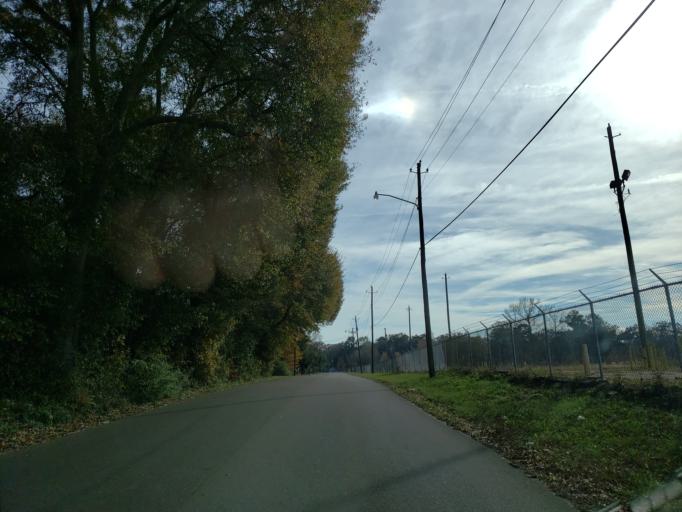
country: US
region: Mississippi
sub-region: Forrest County
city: Hattiesburg
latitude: 31.3379
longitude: -89.3043
